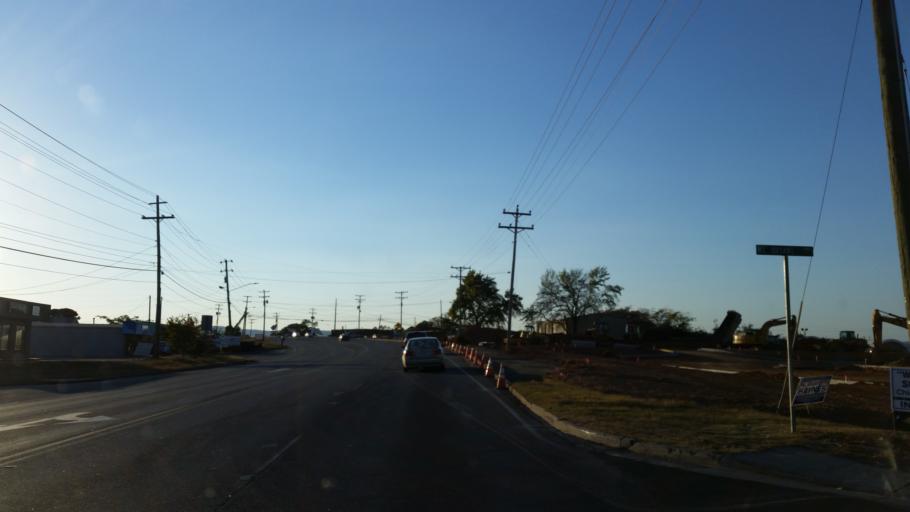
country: US
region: Georgia
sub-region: Gordon County
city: Calhoun
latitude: 34.4815
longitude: -84.9471
